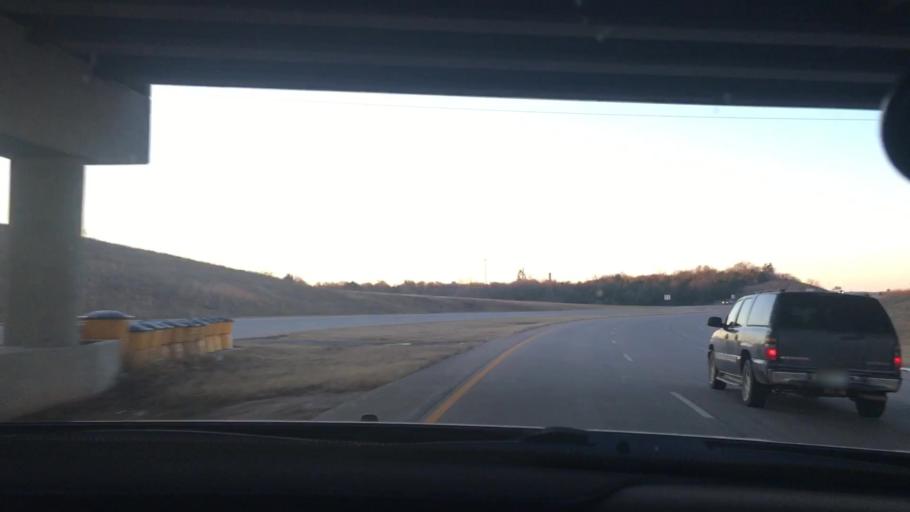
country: US
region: Oklahoma
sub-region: Pontotoc County
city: Ada
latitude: 34.7894
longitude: -96.6933
